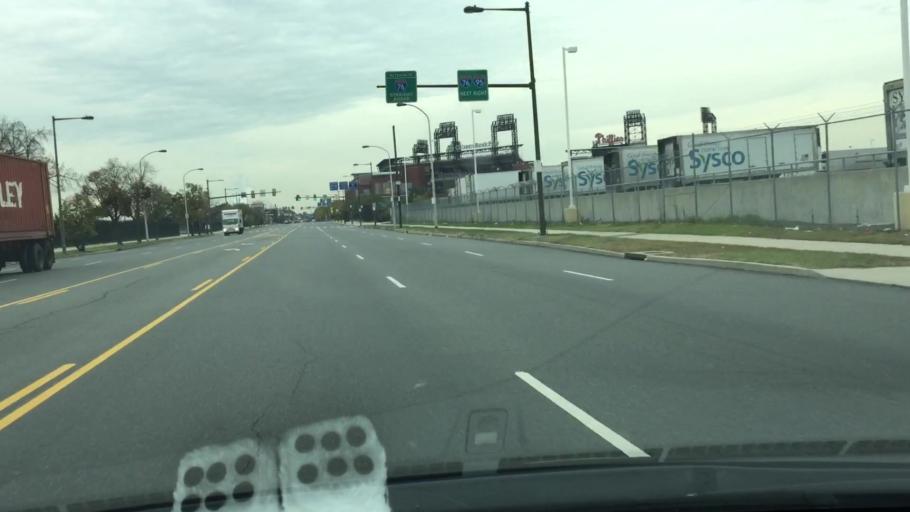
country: US
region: New Jersey
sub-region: Gloucester County
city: National Park
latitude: 39.9037
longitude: -75.1602
